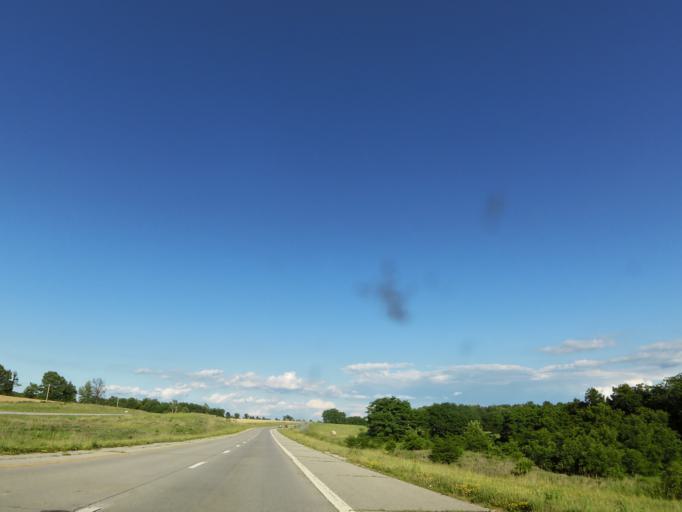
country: US
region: Missouri
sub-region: Pike County
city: Bowling Green
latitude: 39.2593
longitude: -91.0615
